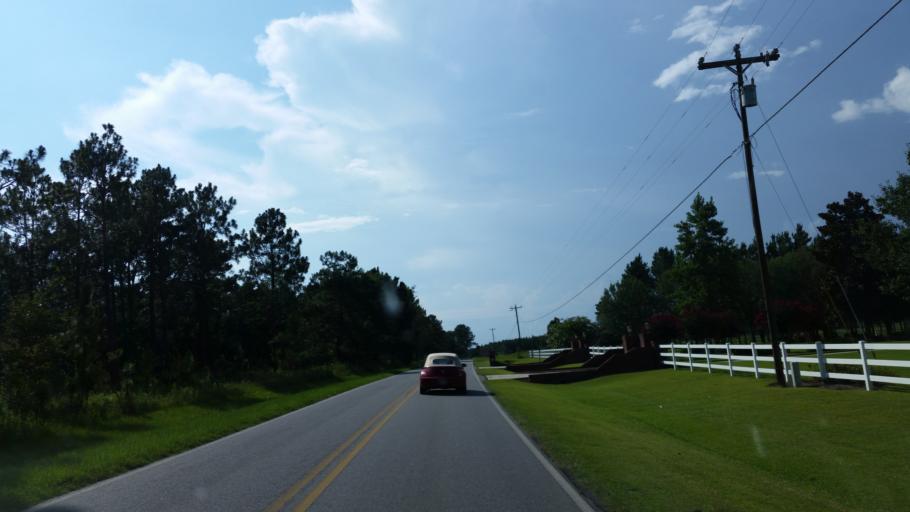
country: US
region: Georgia
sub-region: Lowndes County
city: Hahira
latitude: 30.9322
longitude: -83.4055
